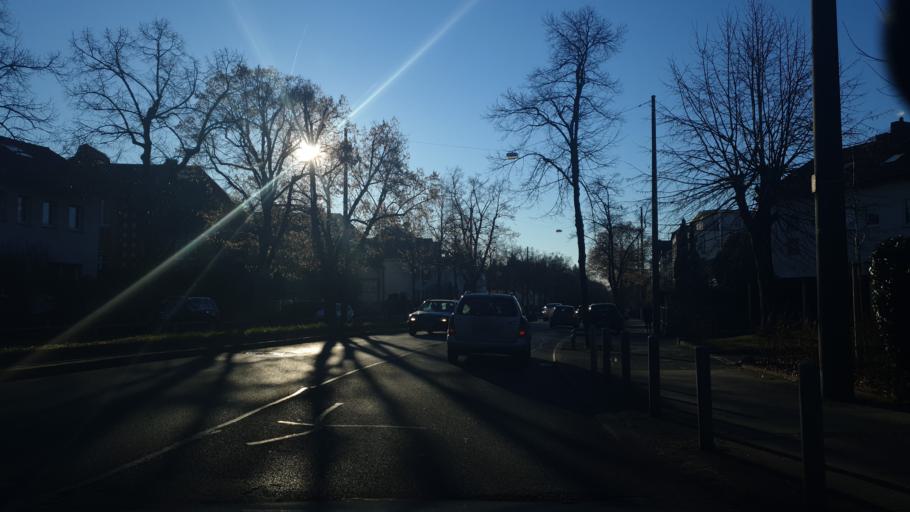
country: DE
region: Hesse
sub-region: Regierungsbezirk Darmstadt
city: Wiesbaden
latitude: 50.0920
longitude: 8.2269
